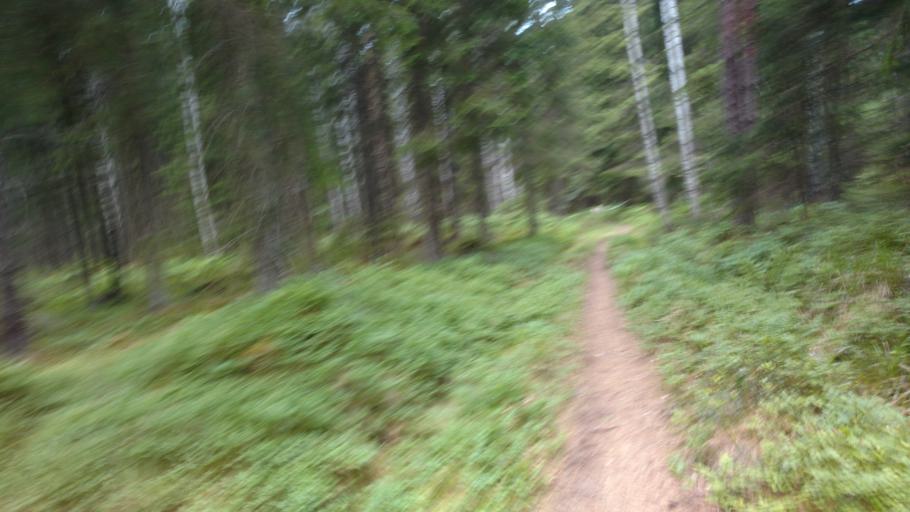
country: FI
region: Uusimaa
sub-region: Raaseporin
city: Pohja
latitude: 60.1178
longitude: 23.5660
